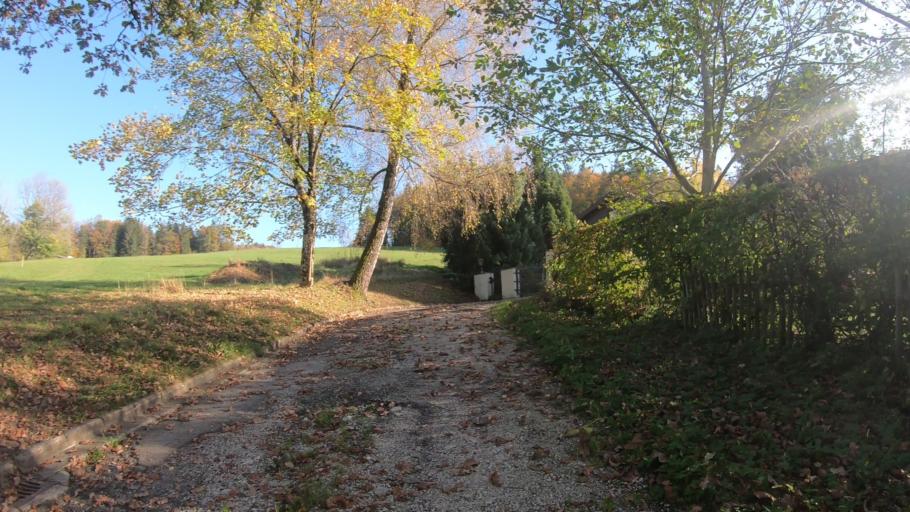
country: DE
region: Bavaria
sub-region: Upper Bavaria
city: Bergen
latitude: 47.8110
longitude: 12.5935
